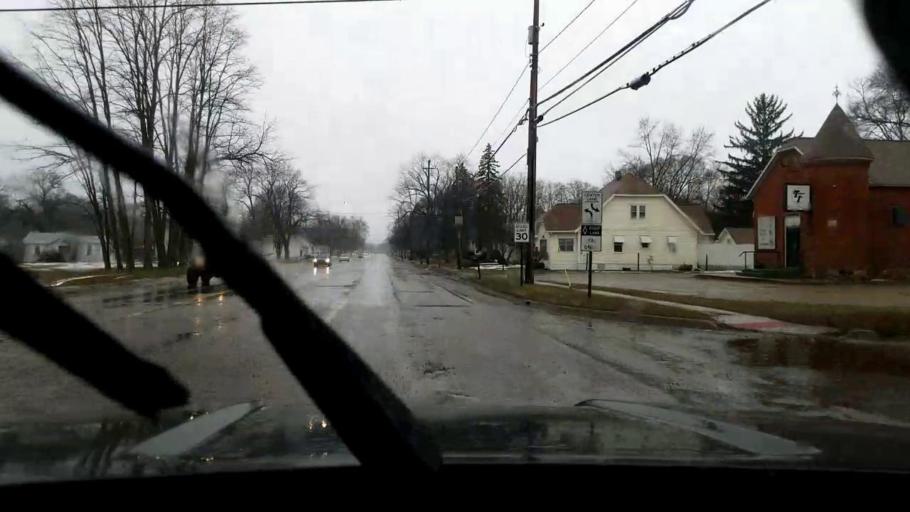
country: US
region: Michigan
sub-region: Jackson County
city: Vandercook Lake
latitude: 42.1969
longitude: -84.3837
